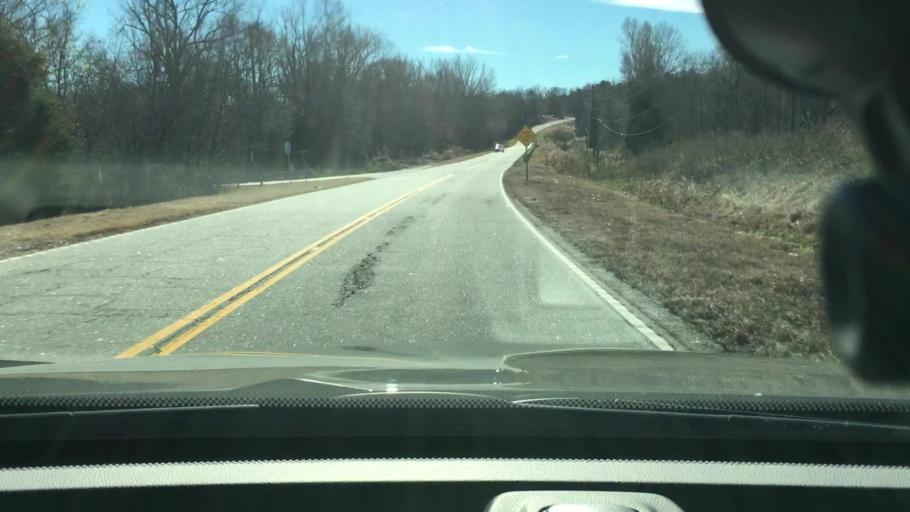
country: US
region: South Carolina
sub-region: Cherokee County
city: Gaffney
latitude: 34.9932
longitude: -81.6912
